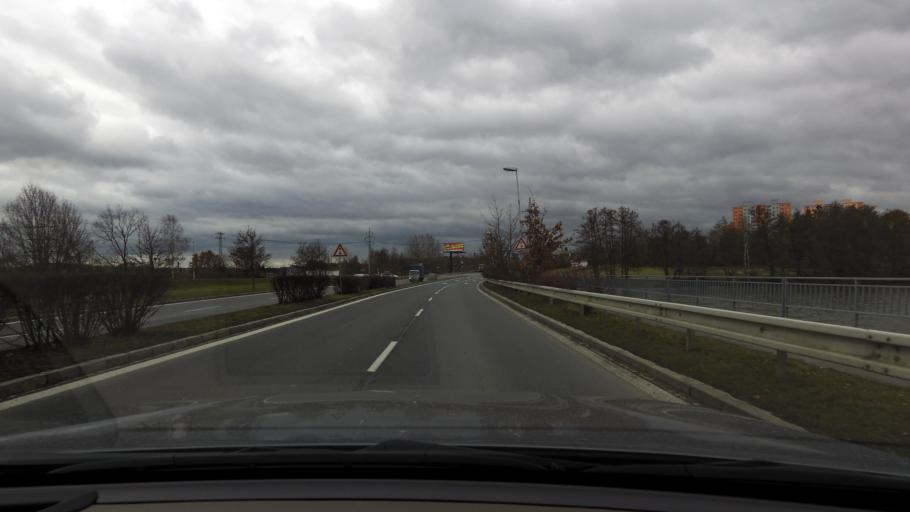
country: CZ
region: Plzensky
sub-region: Okres Plzen-Sever
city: Tremosna
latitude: 49.7868
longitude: 13.3846
